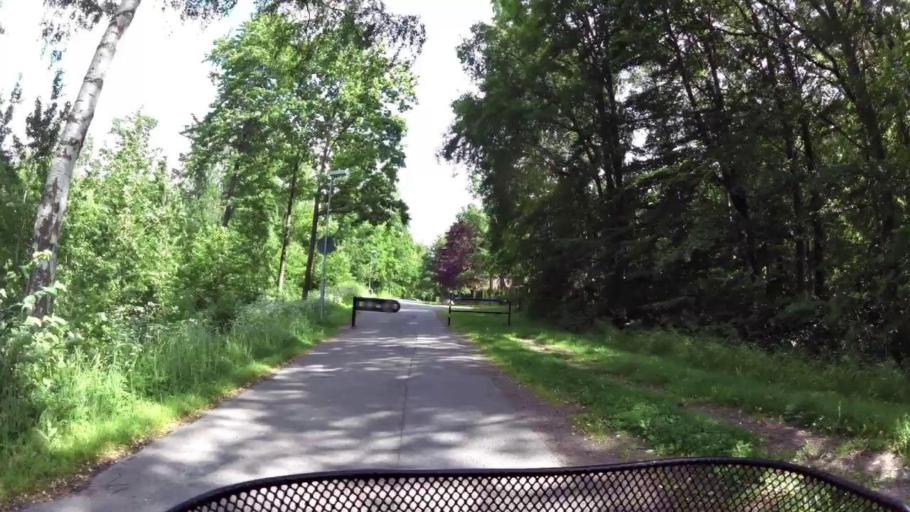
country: SE
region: OEstergoetland
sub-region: Linkopings Kommun
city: Malmslatt
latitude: 58.4193
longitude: 15.5069
